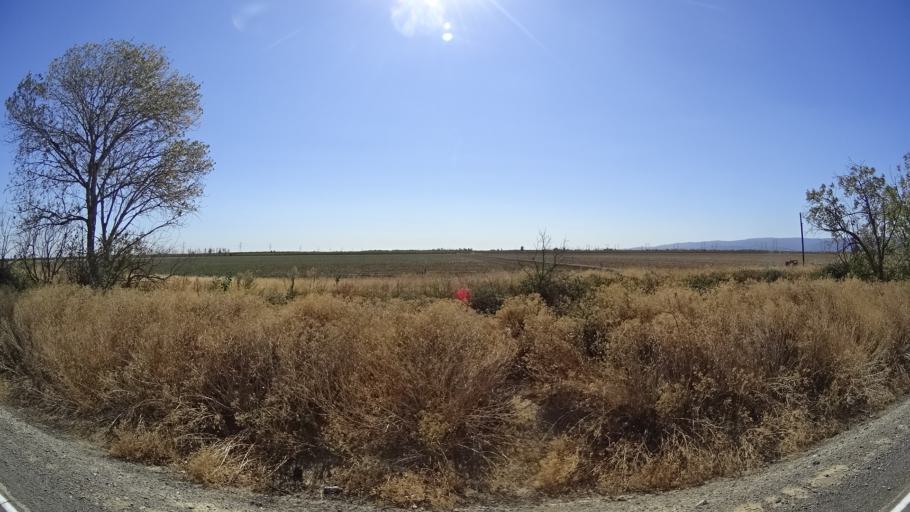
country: US
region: California
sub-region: Yolo County
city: Winters
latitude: 38.5620
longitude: -121.9155
